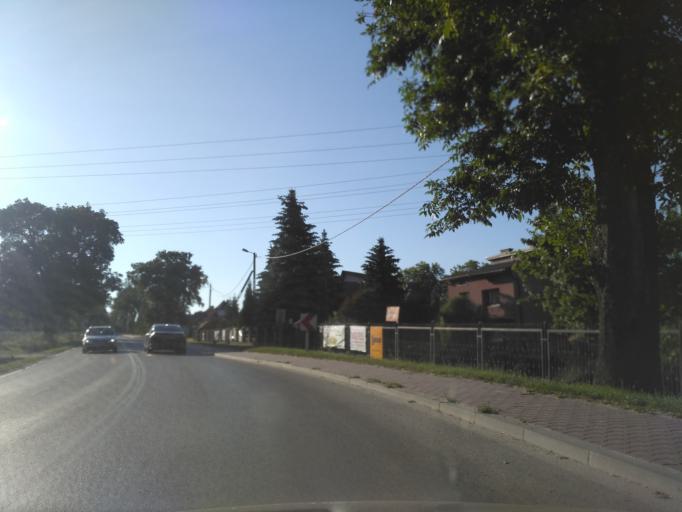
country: PL
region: Lublin Voivodeship
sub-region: Powiat lubelski
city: Bychawa
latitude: 51.0193
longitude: 22.5235
